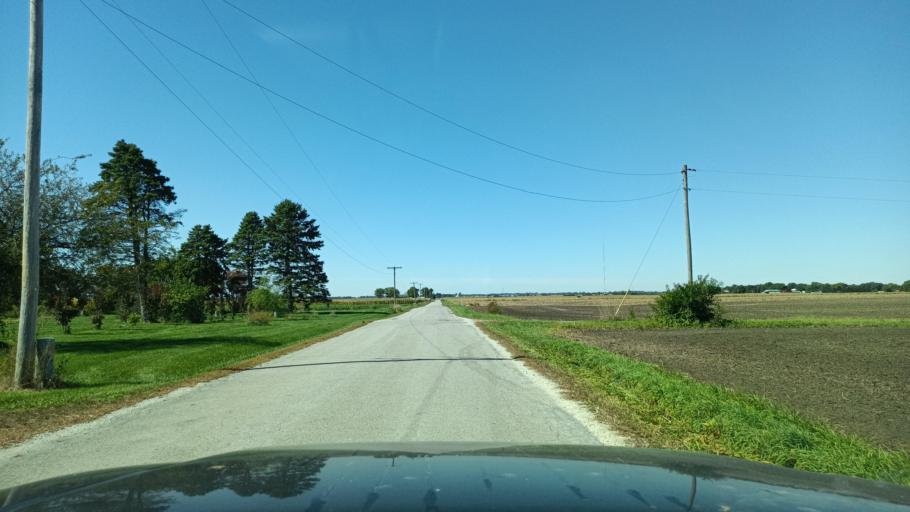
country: US
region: Illinois
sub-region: Champaign County
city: Mahomet
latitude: 40.0987
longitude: -88.4102
